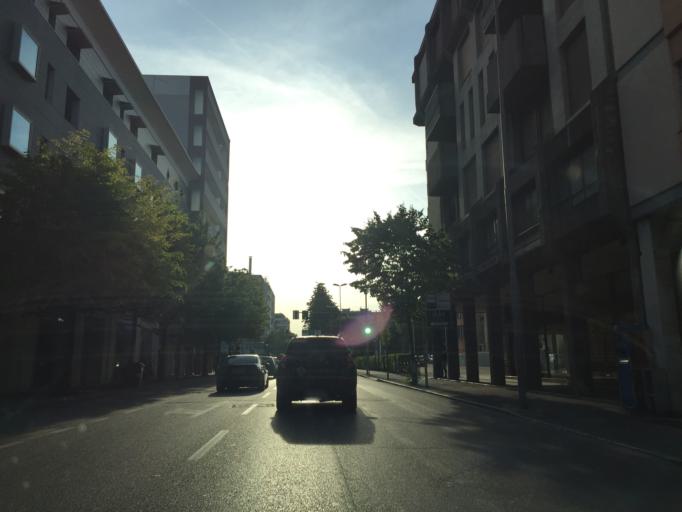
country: IT
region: Friuli Venezia Giulia
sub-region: Provincia di Pordenone
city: Pordenone
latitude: 45.9621
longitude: 12.6586
